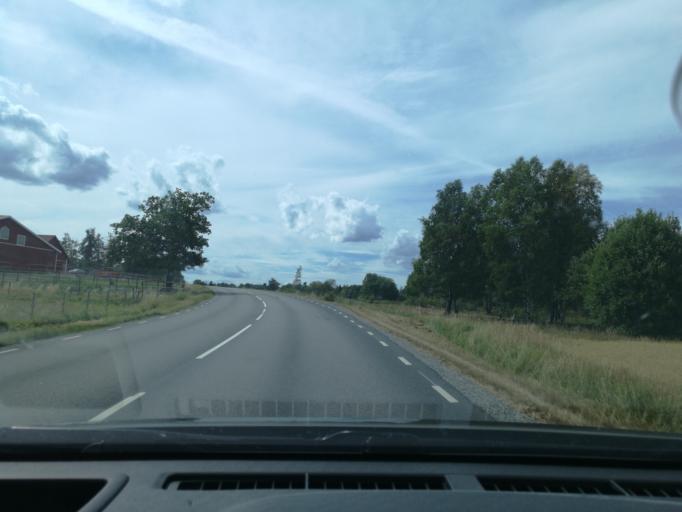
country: SE
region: Stockholm
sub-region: Sigtuna Kommun
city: Rosersberg
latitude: 59.5893
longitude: 17.8861
